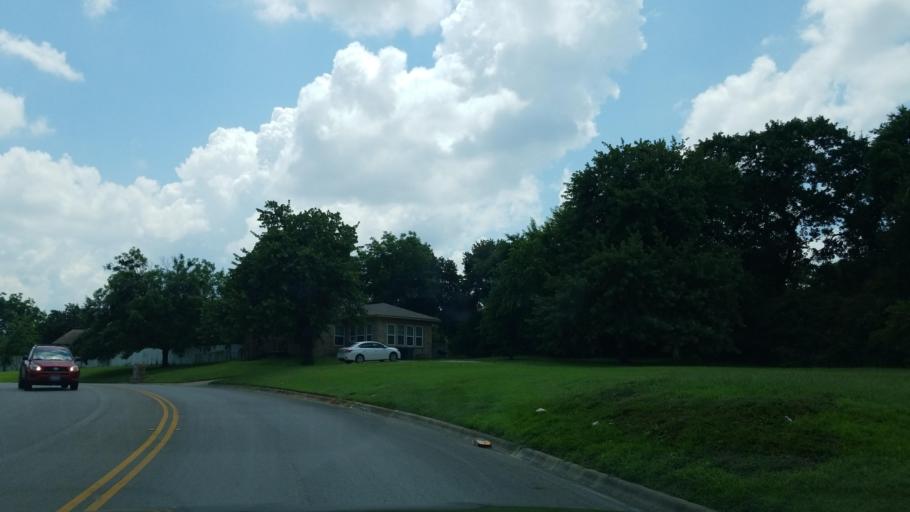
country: US
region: Texas
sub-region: Denton County
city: Denton
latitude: 33.2062
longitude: -97.1242
